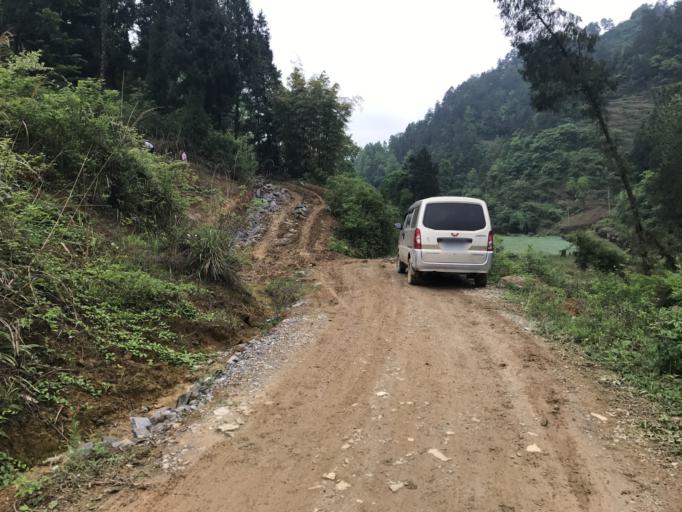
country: CN
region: Guizhou Sheng
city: Xujiaba
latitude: 27.7298
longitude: 108.0170
